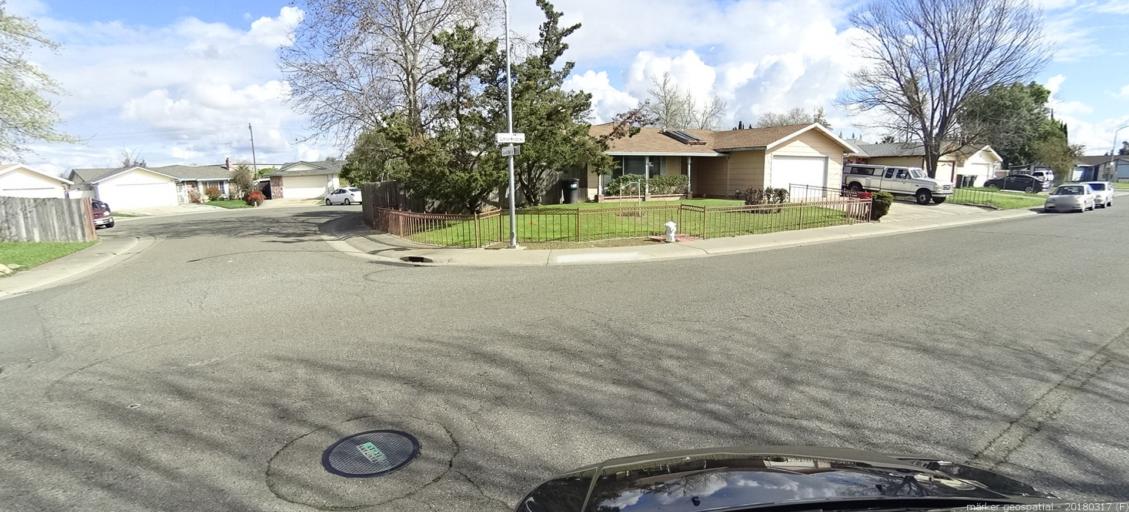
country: US
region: California
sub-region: Sacramento County
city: Florin
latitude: 38.4732
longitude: -121.3961
